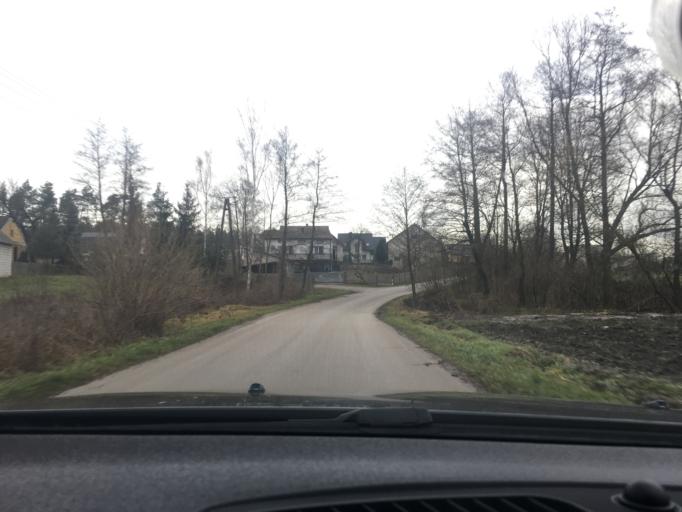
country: PL
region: Swietokrzyskie
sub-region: Powiat jedrzejowski
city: Imielno
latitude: 50.6398
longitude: 20.4158
